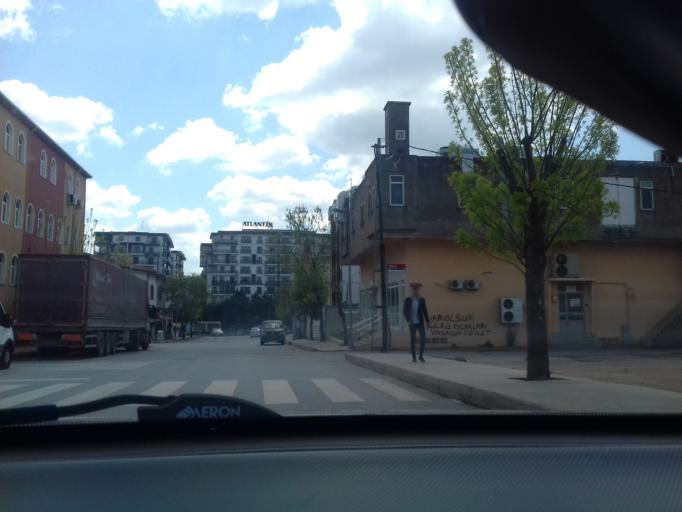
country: TR
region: Istanbul
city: Pendik
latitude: 40.8937
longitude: 29.2759
